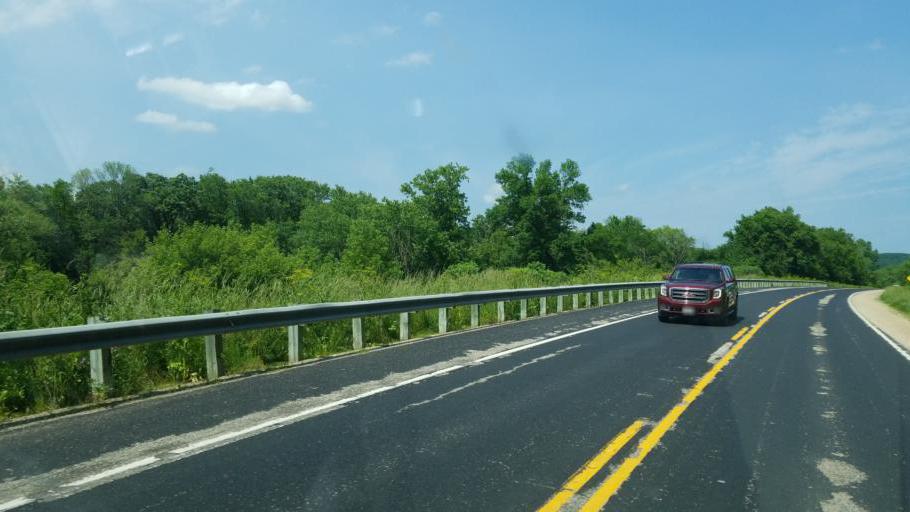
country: US
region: Wisconsin
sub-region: Monroe County
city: Cashton
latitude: 43.5637
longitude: -90.6400
